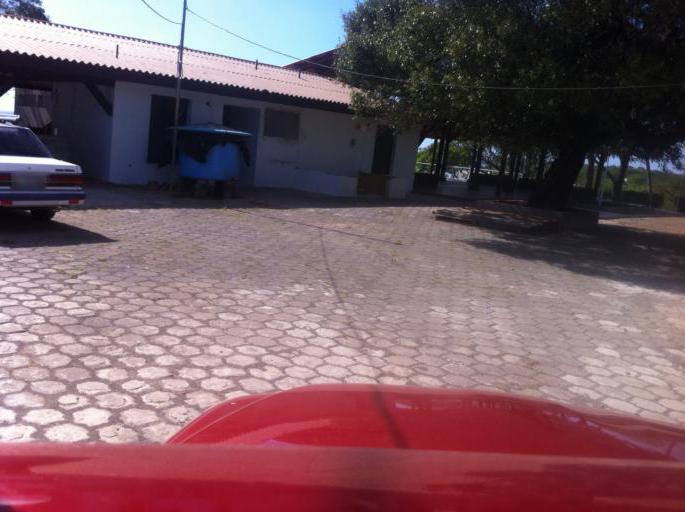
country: NI
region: Carazo
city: Santa Teresa
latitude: 11.6164
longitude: -86.3235
